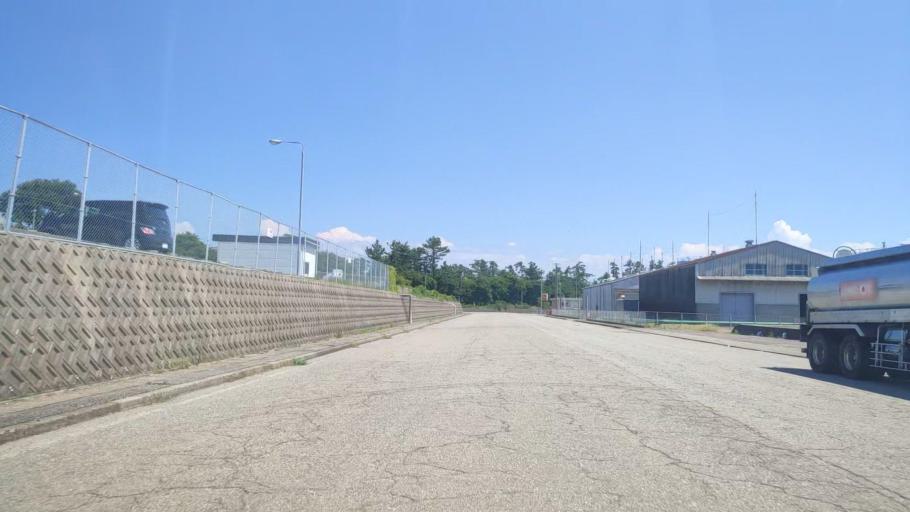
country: JP
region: Ishikawa
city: Kanazawa-shi
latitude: 36.6196
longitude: 136.6127
